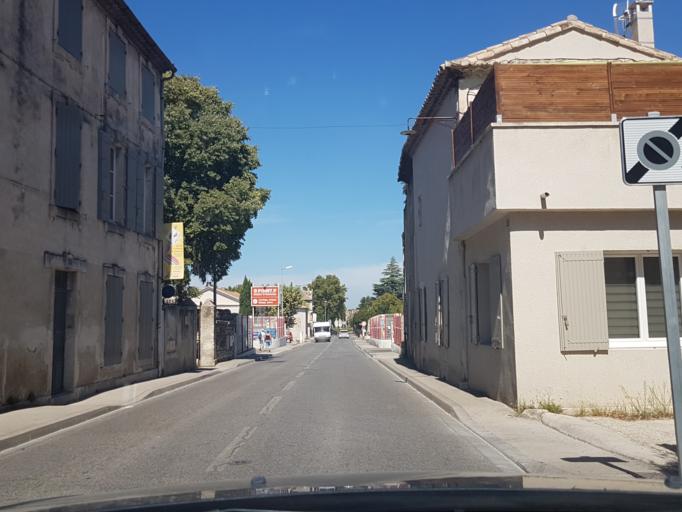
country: FR
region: Provence-Alpes-Cote d'Azur
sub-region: Departement des Bouches-du-Rhone
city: Saint-Remy-de-Provence
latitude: 43.7908
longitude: 4.8333
